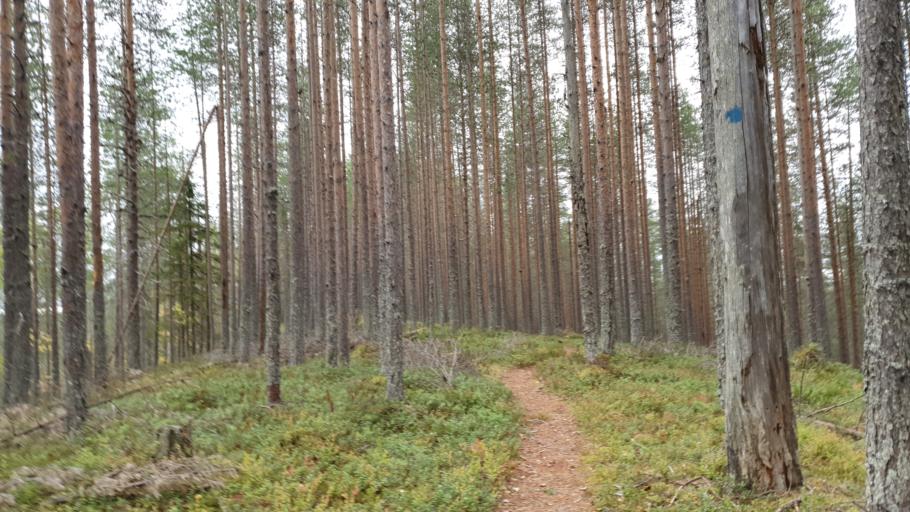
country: FI
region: Kainuu
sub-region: Kehys-Kainuu
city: Kuhmo
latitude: 64.2933
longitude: 29.3347
